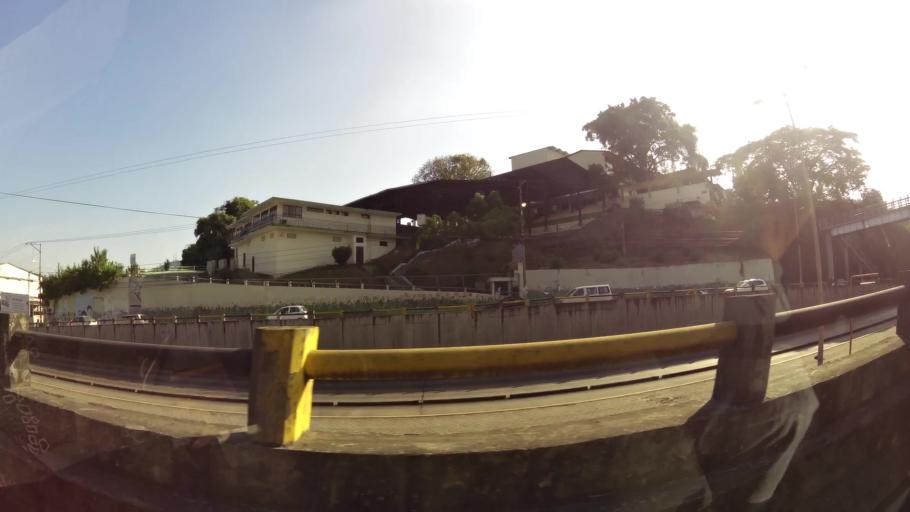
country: EC
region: Guayas
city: Guayaquil
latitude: -2.1490
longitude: -79.9326
